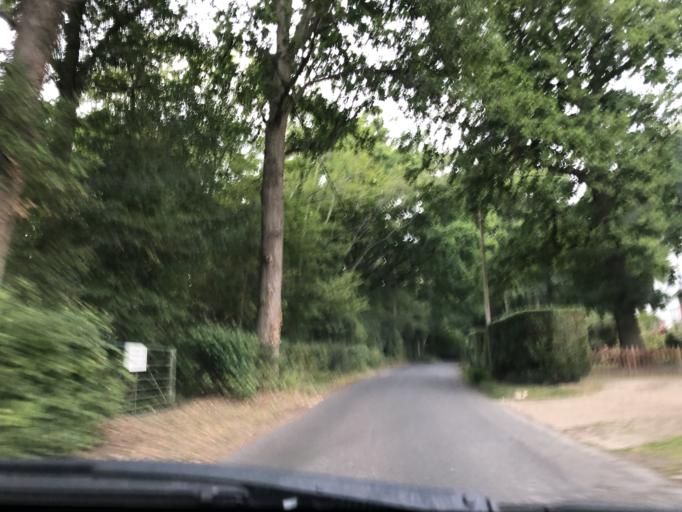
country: GB
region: England
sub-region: Kent
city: Sevenoaks
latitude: 51.2386
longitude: 0.2344
